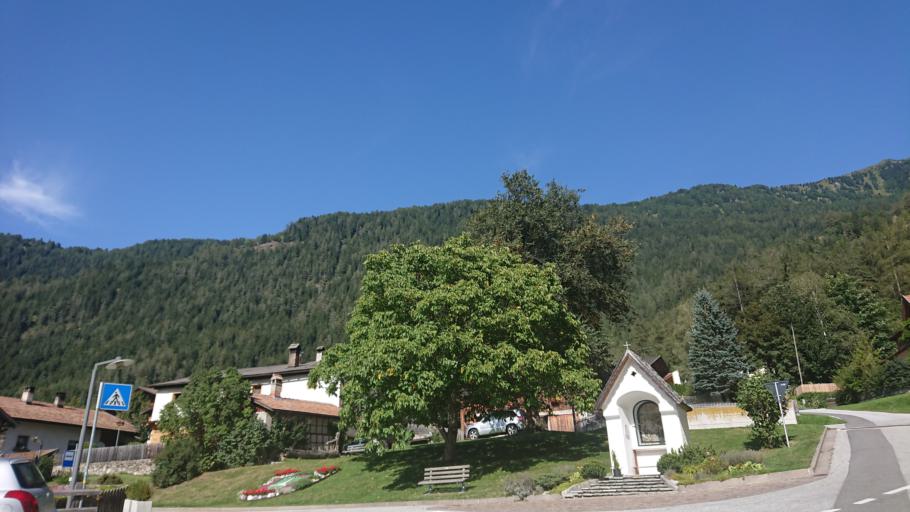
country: IT
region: Trentino-Alto Adige
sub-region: Bolzano
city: Campo di Trens
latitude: 46.8746
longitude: 11.4866
